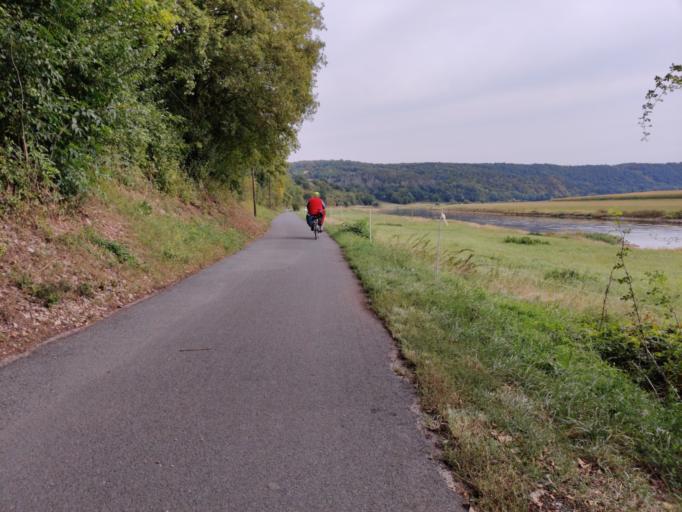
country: DE
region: Lower Saxony
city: Hehlen
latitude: 51.9902
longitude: 9.4741
